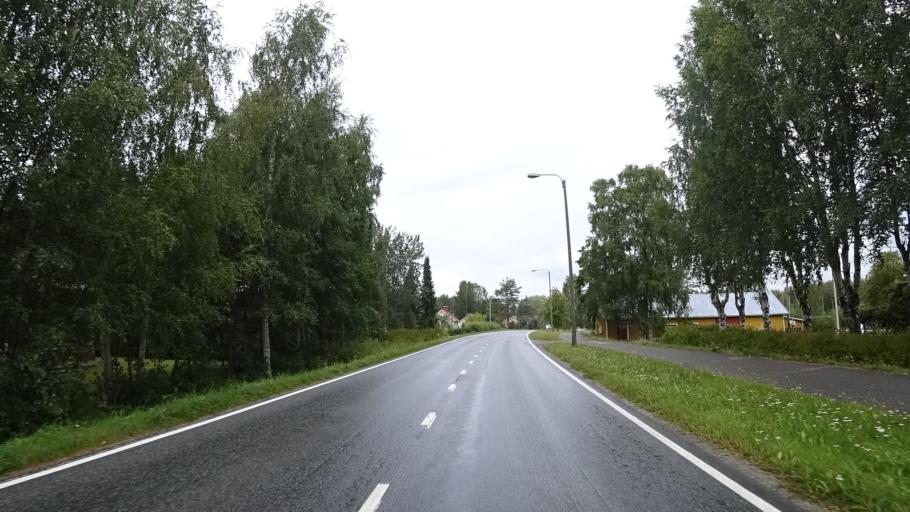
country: FI
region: Southern Savonia
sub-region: Savonlinna
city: Kerimaeki
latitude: 61.9230
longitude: 29.2784
